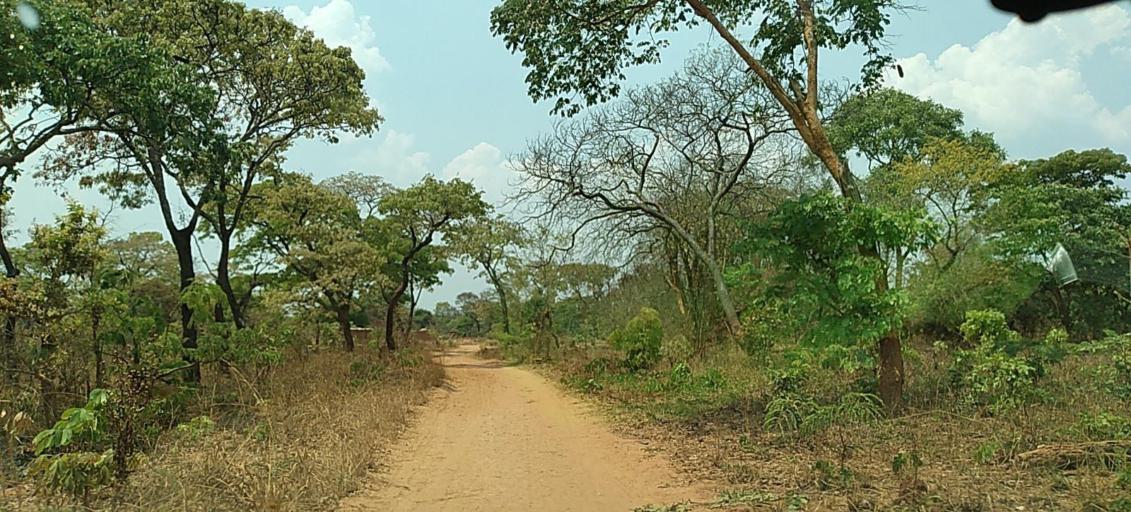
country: ZM
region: North-Western
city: Kabompo
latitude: -13.6437
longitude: 24.3788
